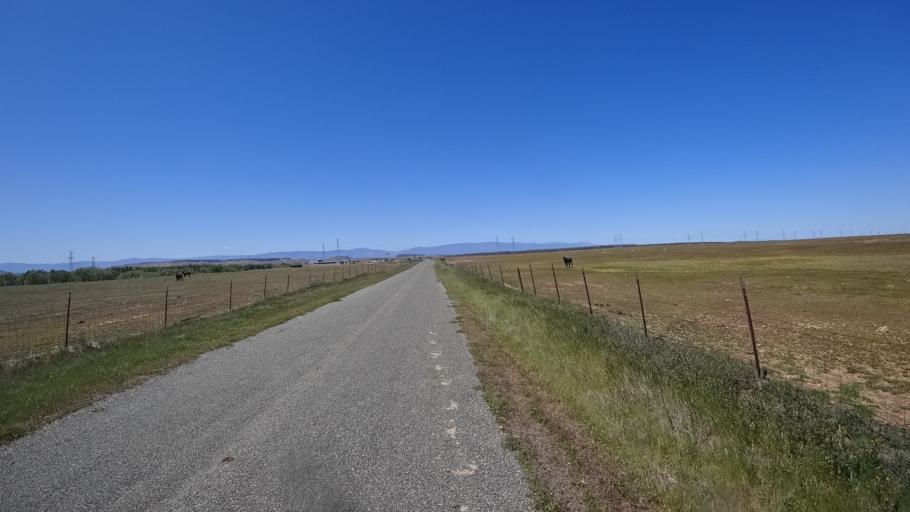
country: US
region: California
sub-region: Glenn County
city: Orland
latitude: 39.8003
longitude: -122.2667
